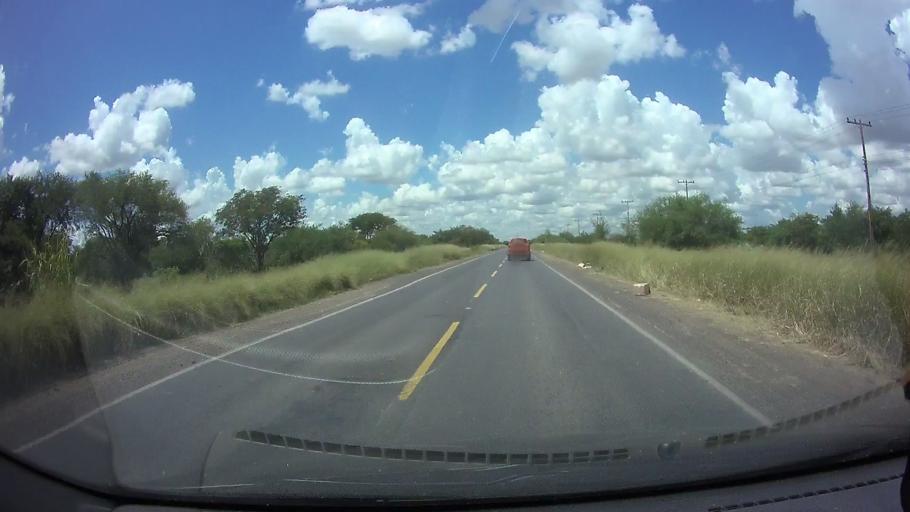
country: PY
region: Central
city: Colonia Mariano Roque Alonso
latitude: -25.1891
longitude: -57.6100
